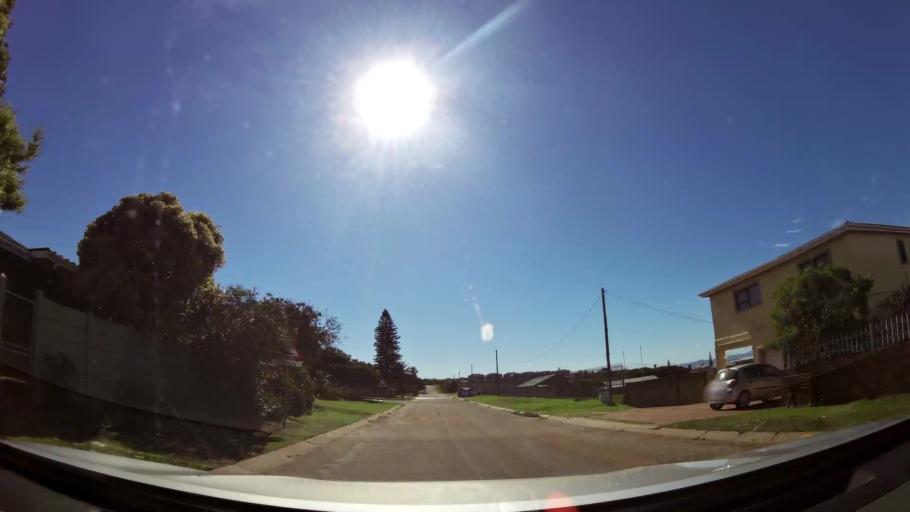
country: ZA
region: Eastern Cape
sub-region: Cacadu District Municipality
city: Jeffrey's Bay
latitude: -34.0515
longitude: 24.9169
